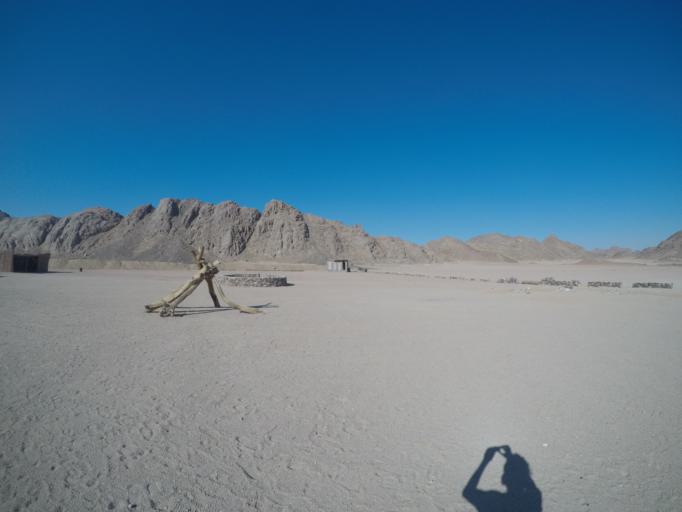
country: EG
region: Red Sea
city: El Gouna
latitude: 27.1528
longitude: 33.5433
